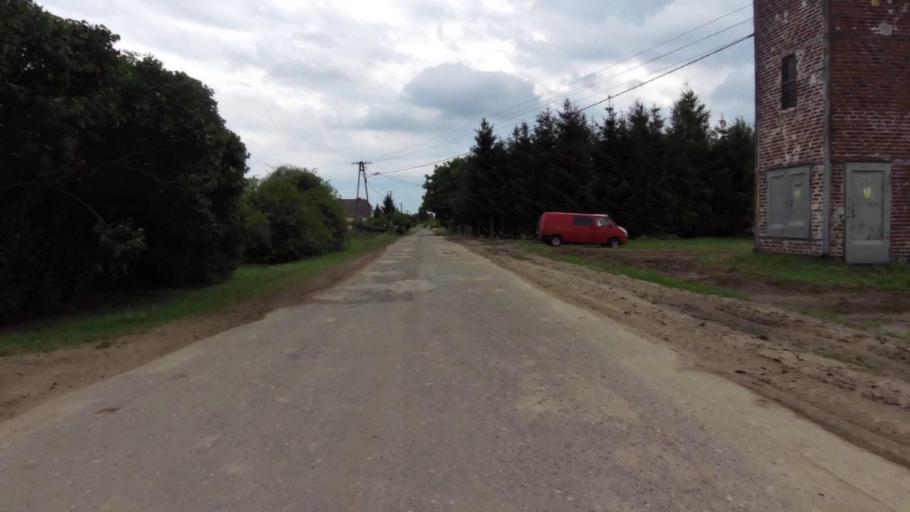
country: PL
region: West Pomeranian Voivodeship
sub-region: Powiat pyrzycki
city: Lipiany
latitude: 52.9647
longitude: 14.9548
